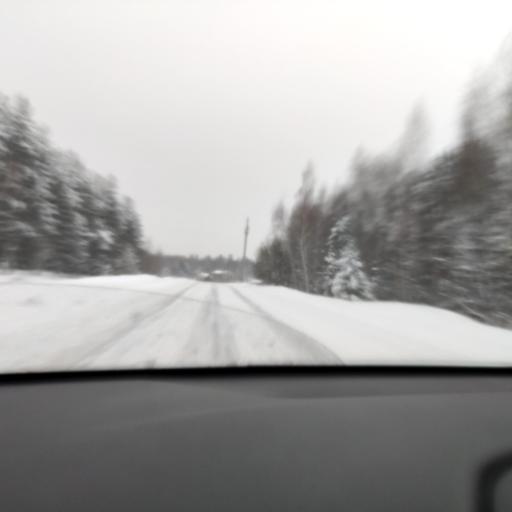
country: RU
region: Tatarstan
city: Vysokaya Gora
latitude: 55.9596
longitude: 49.1603
